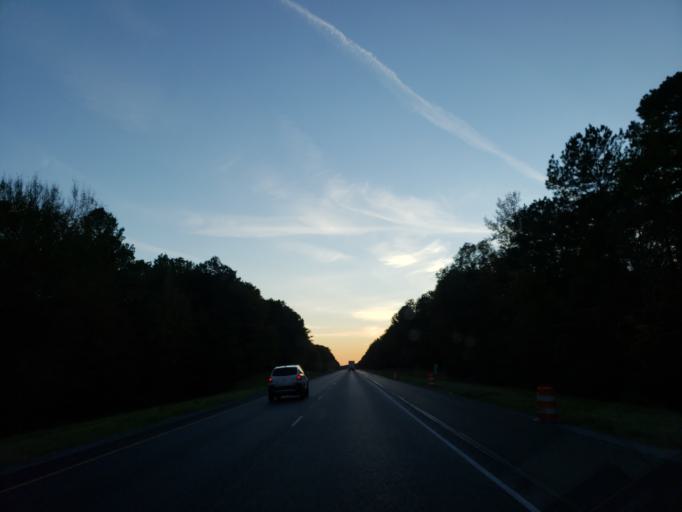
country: US
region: Alabama
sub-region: Sumter County
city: Livingston
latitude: 32.5757
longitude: -88.2422
